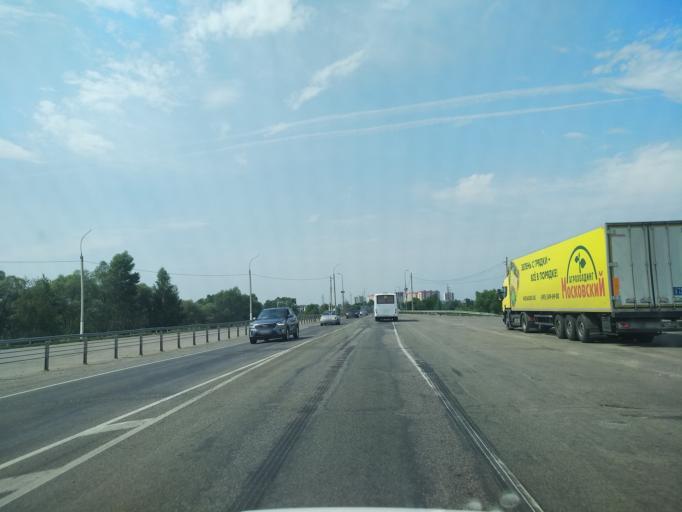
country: RU
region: Voronezj
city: Somovo
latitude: 51.6807
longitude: 39.3427
